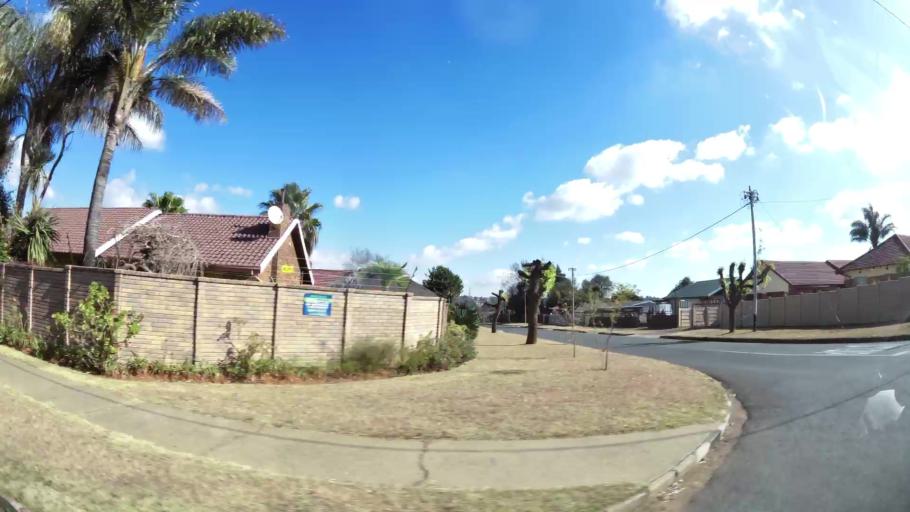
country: ZA
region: Gauteng
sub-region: City of Johannesburg Metropolitan Municipality
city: Roodepoort
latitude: -26.1321
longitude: 27.8322
